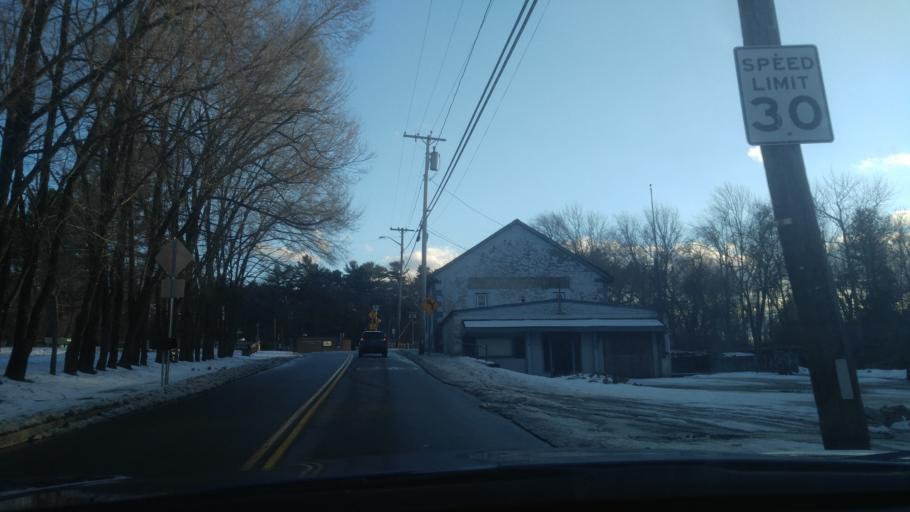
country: US
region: Rhode Island
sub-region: Kent County
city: Coventry
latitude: 41.7017
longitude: -71.6354
